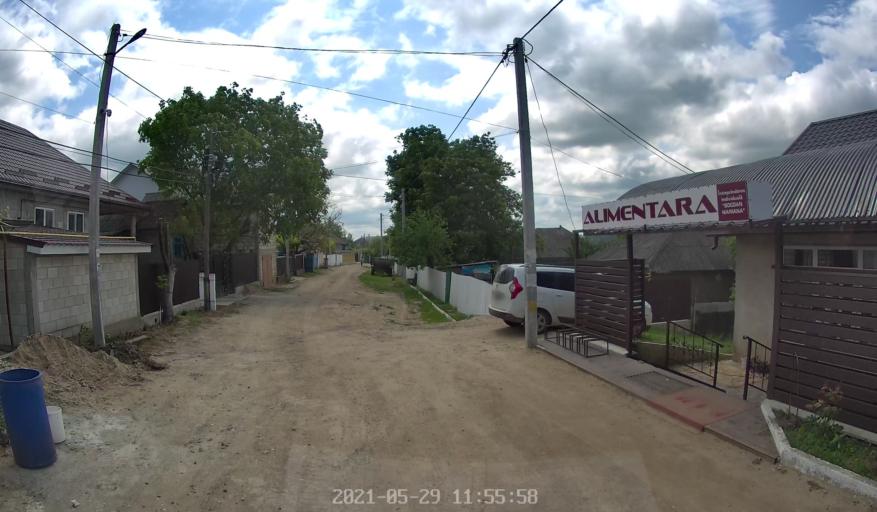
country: MD
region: Hincesti
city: Hincesti
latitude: 46.8819
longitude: 28.6291
